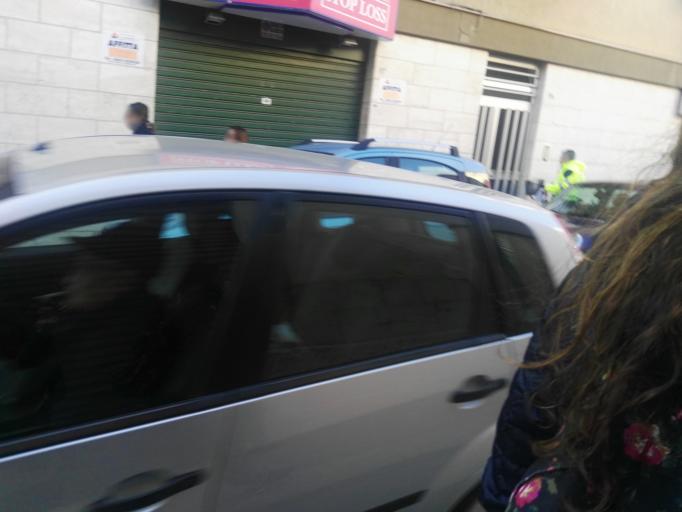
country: IT
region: Apulia
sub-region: Provincia di Barletta - Andria - Trani
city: Andria
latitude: 41.2285
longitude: 16.3015
